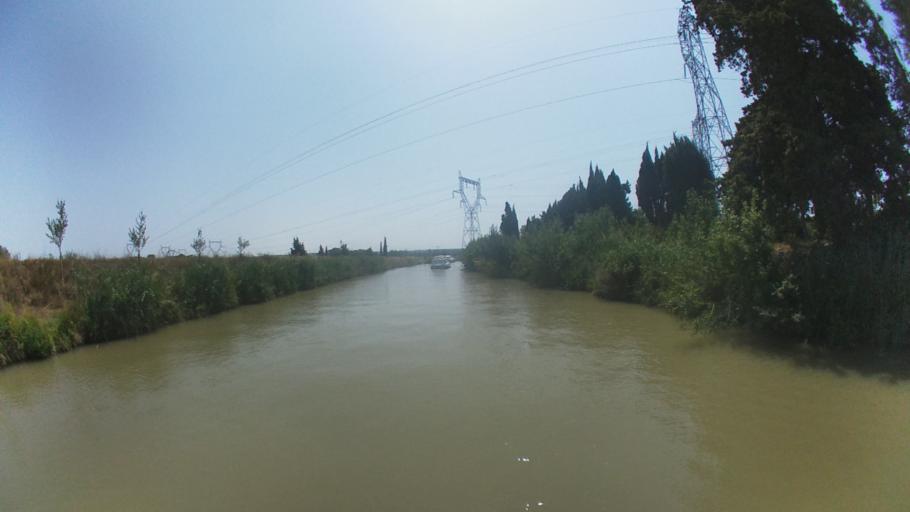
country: FR
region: Languedoc-Roussillon
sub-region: Departement de l'Aude
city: Azille
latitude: 43.2460
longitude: 2.6605
